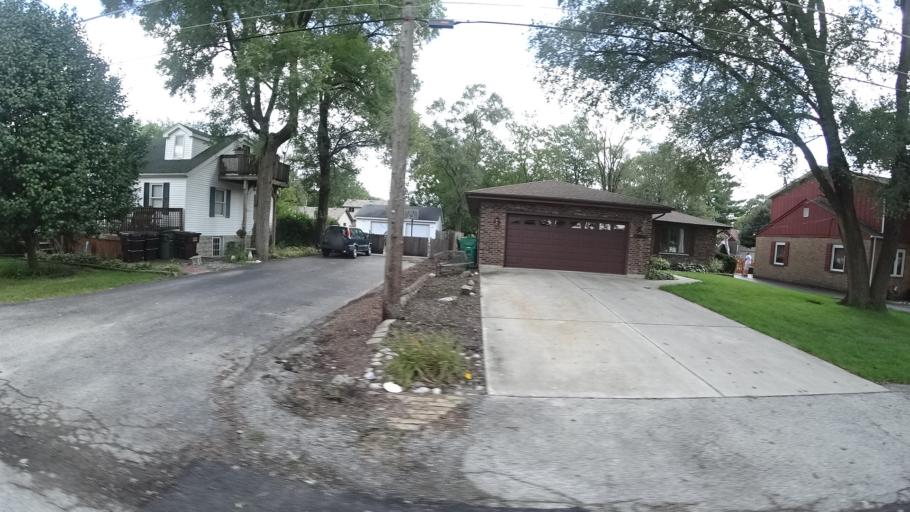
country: US
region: Illinois
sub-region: Cook County
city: Tinley Park
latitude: 41.5681
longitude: -87.7829
